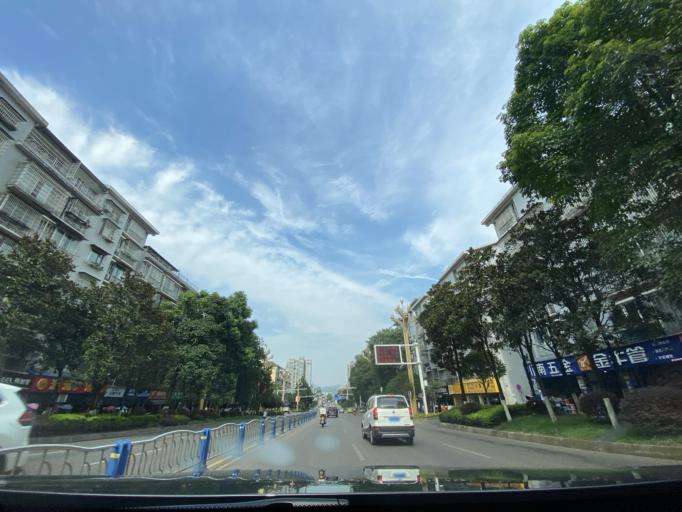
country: CN
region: Sichuan
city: Fuji
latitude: 29.1530
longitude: 105.3590
